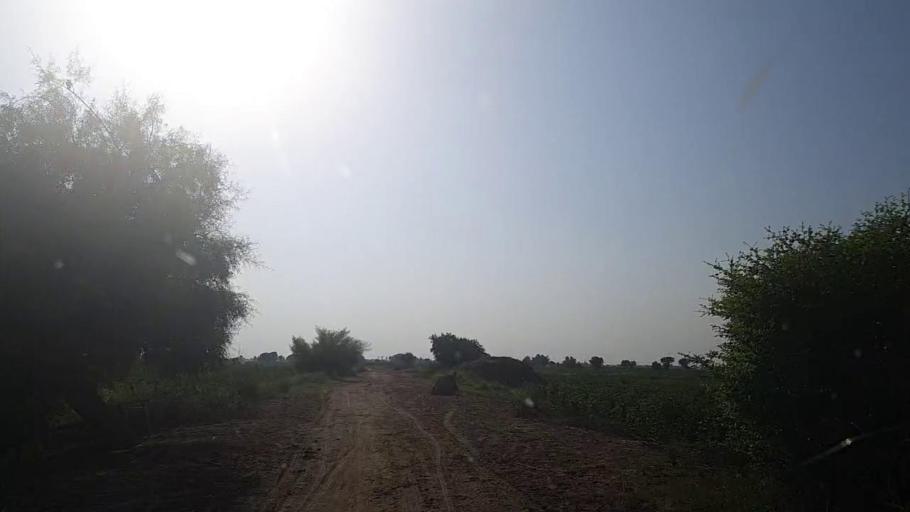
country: PK
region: Sindh
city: Khanpur
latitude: 27.7306
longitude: 69.3285
